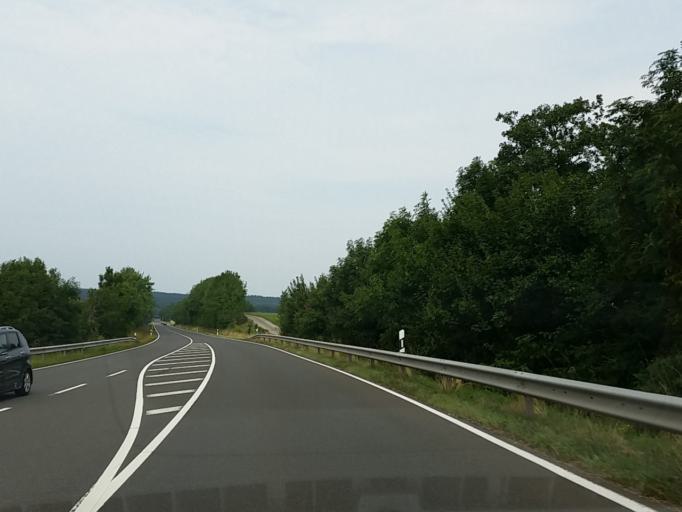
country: DE
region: Rheinland-Pfalz
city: Reinsfeld
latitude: 49.6822
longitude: 6.8958
